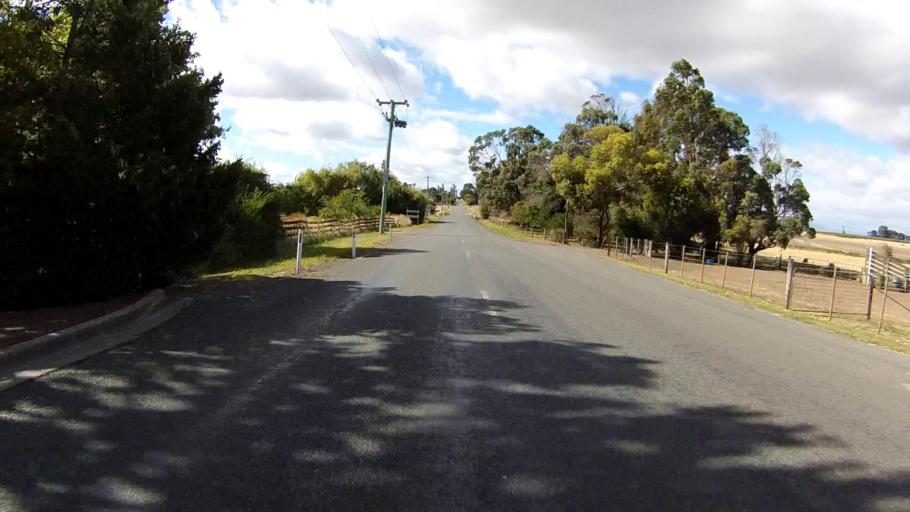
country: AU
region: Tasmania
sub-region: Northern Midlands
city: Evandale
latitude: -41.5735
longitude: 147.2489
